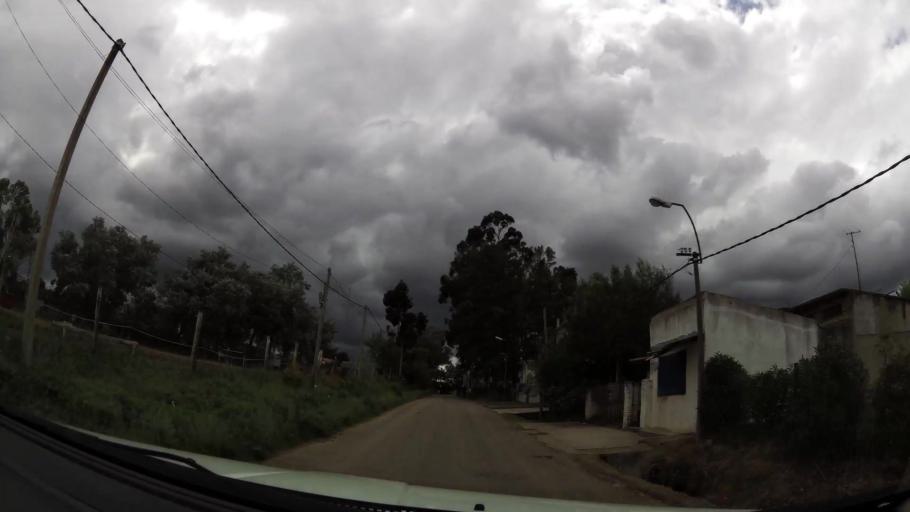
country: UY
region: Canelones
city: Toledo
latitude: -34.8009
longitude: -56.1281
